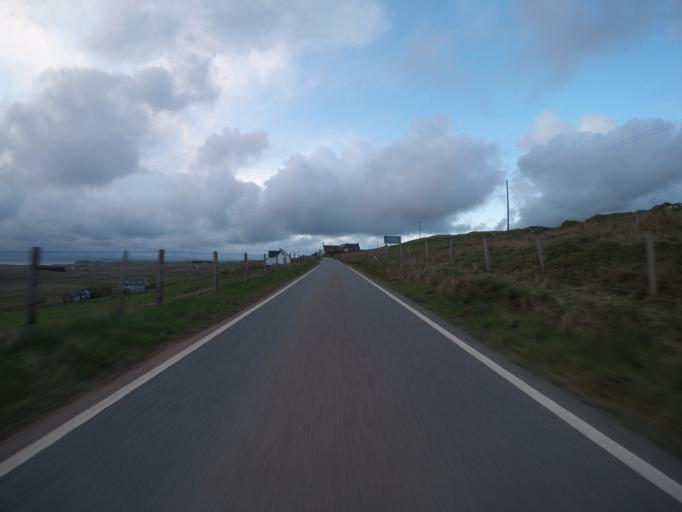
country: GB
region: Scotland
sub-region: Highland
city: Portree
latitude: 57.6335
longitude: -6.3771
